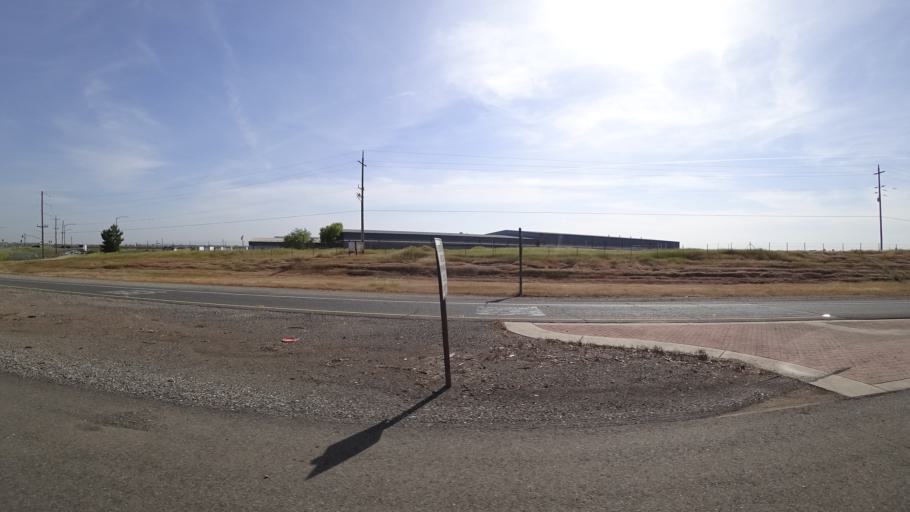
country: US
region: California
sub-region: Butte County
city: Durham
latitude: 39.6449
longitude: -121.7194
